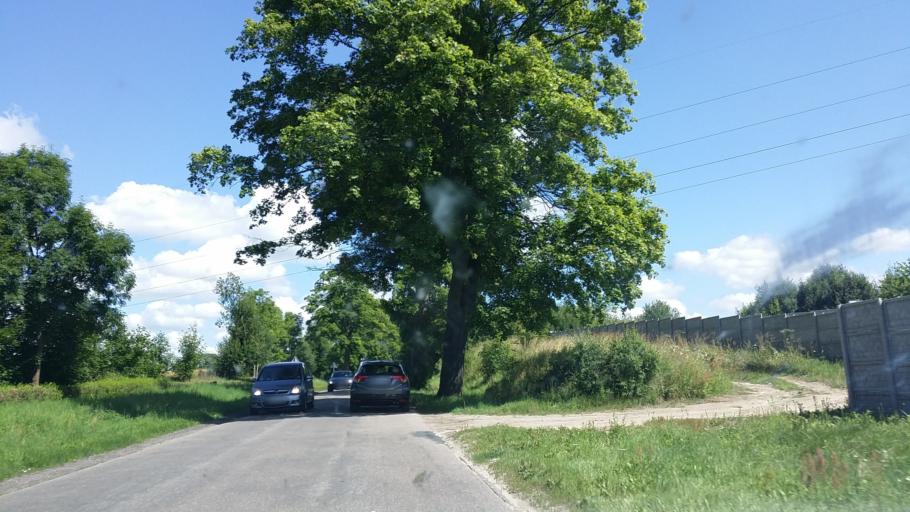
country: PL
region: West Pomeranian Voivodeship
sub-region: Powiat swidwinski
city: Swidwin
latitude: 53.7575
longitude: 15.7646
